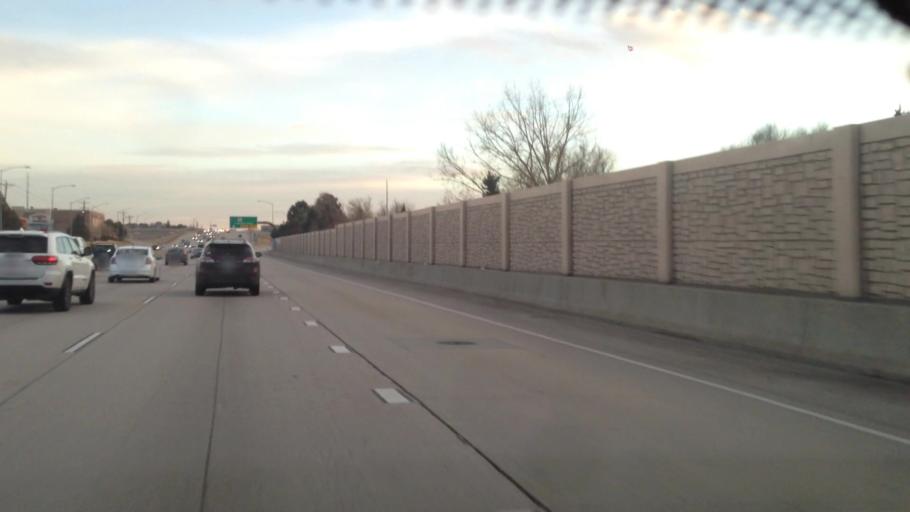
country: US
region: Colorado
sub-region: Arapahoe County
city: Dove Valley
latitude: 39.6004
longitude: -104.8053
